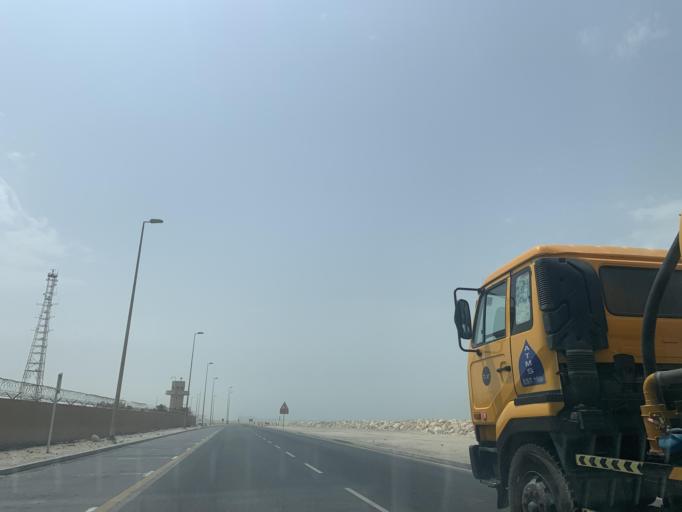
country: BH
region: Muharraq
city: Al Hadd
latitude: 26.2260
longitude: 50.7001
